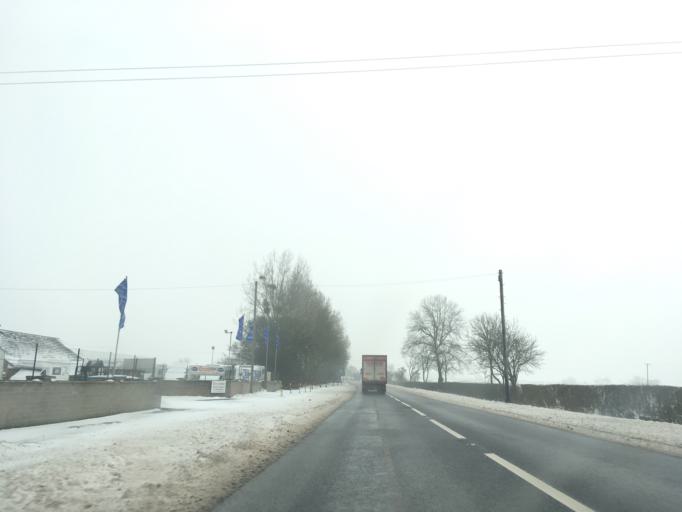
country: GB
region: England
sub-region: Gloucestershire
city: Gotherington
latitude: 52.0174
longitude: -2.0245
